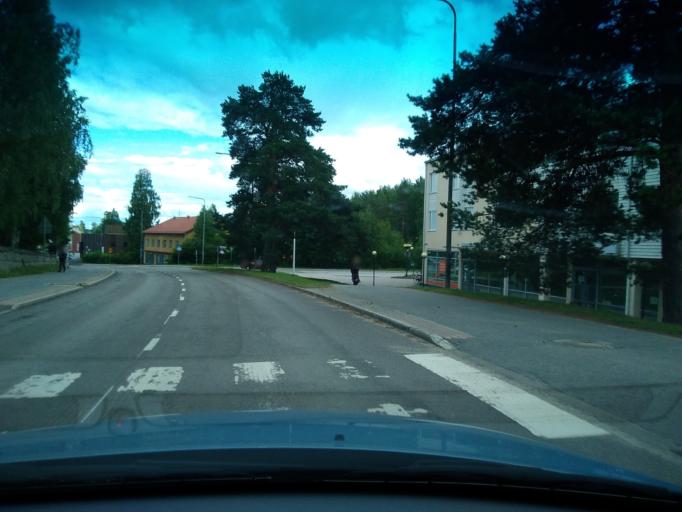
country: FI
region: Central Finland
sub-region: Saarijaervi-Viitasaari
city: Saarijaervi
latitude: 62.7044
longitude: 25.2567
